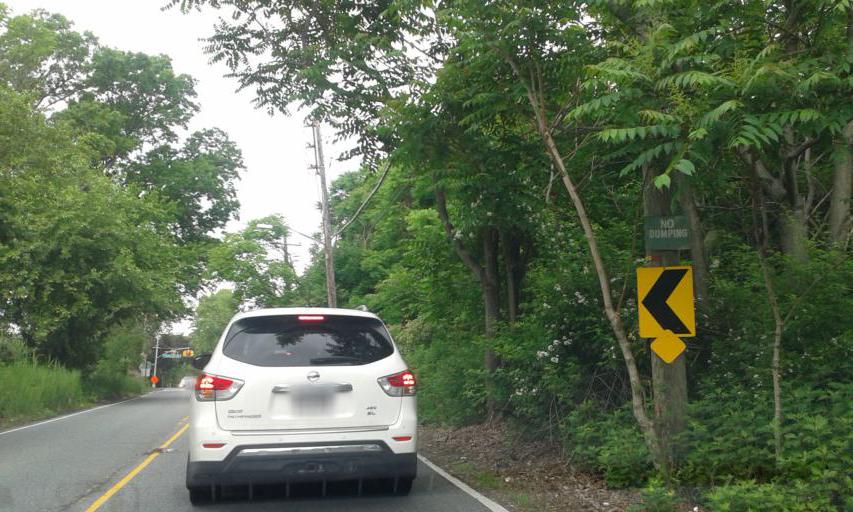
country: US
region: New York
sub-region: Richmond County
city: Staten Island
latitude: 40.5801
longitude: -74.1511
